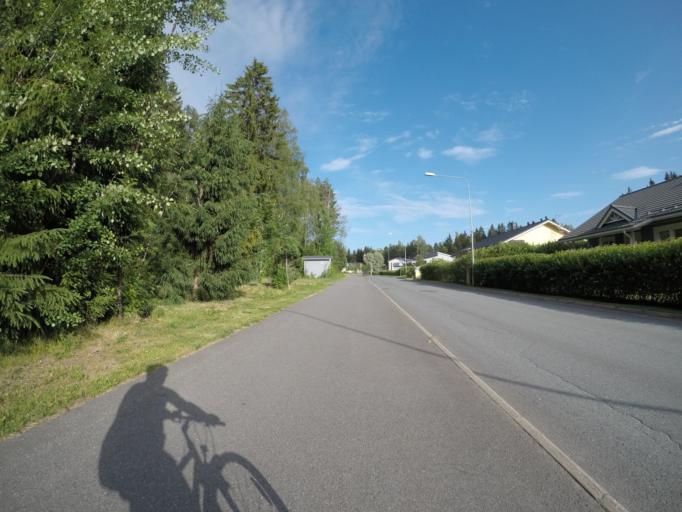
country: FI
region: Haeme
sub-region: Haemeenlinna
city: Parola
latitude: 60.9745
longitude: 24.3874
